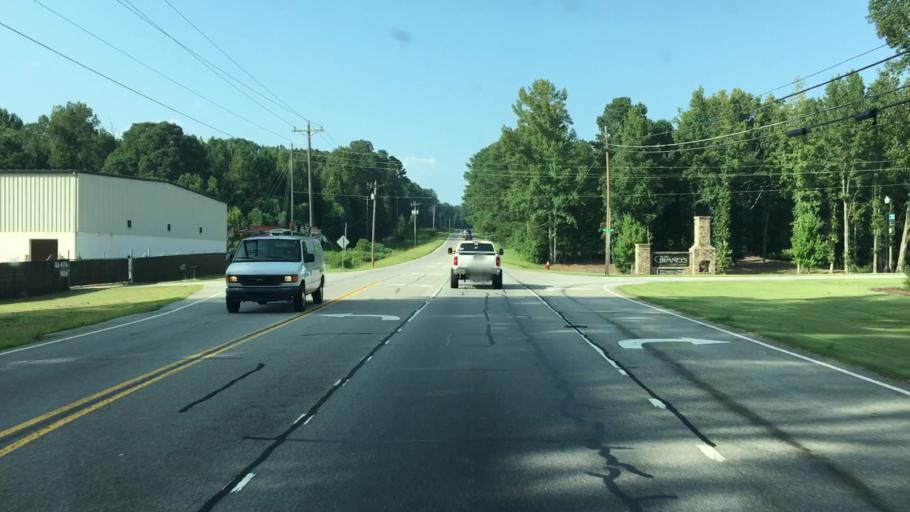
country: US
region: Georgia
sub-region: Barrow County
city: Russell
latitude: 33.9601
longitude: -83.7197
